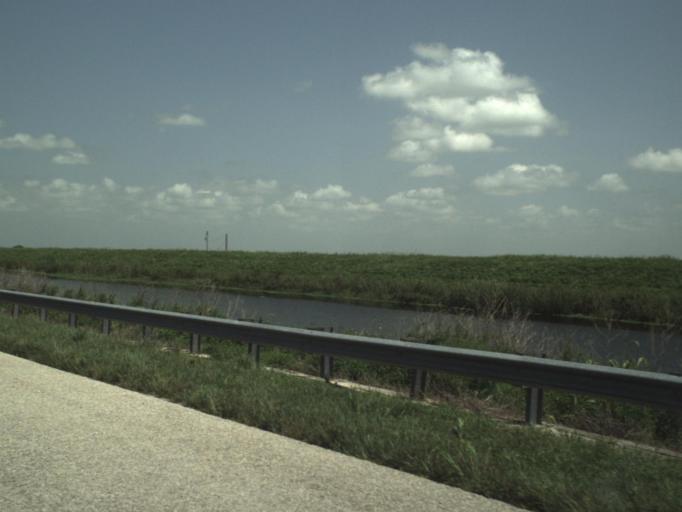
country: US
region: Florida
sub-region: Palm Beach County
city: Belle Glade Camp
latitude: 26.5006
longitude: -80.6660
